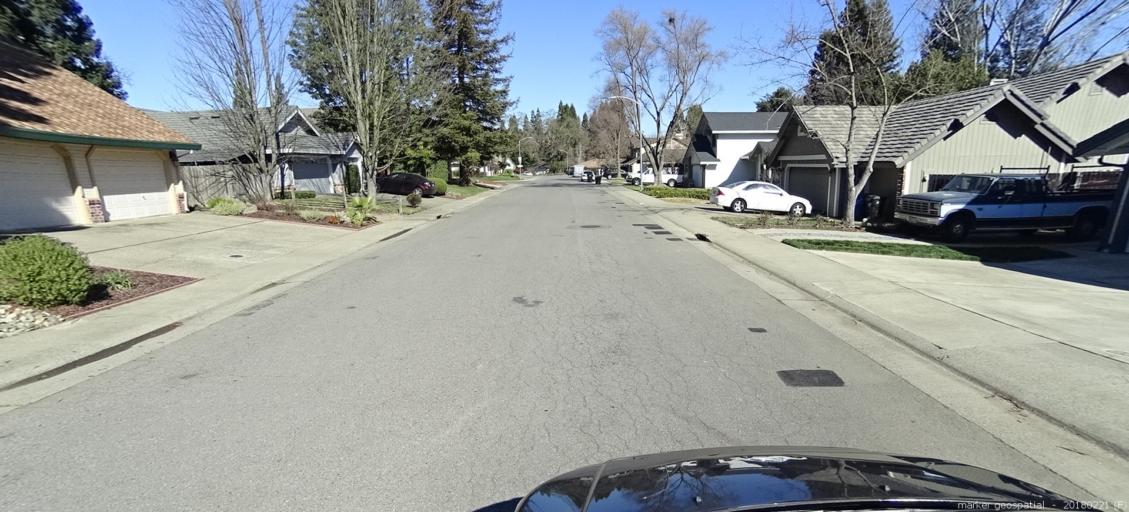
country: US
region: California
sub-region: Sacramento County
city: Orangevale
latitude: 38.6943
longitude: -121.2426
